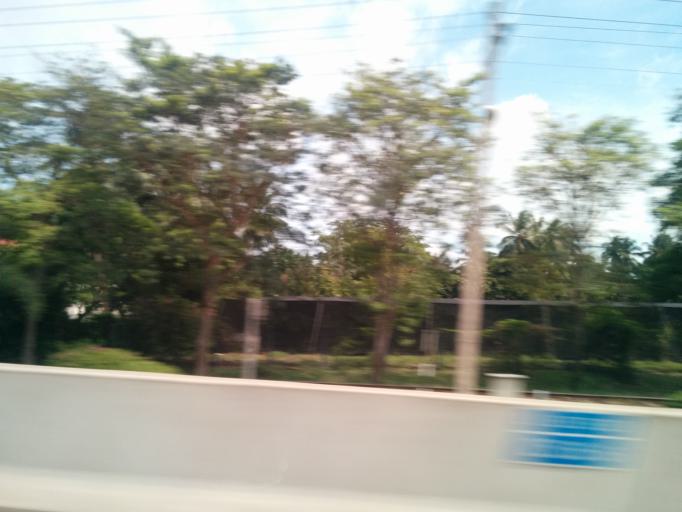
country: LK
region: Western
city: Katunayaka
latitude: 7.1614
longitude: 79.8771
